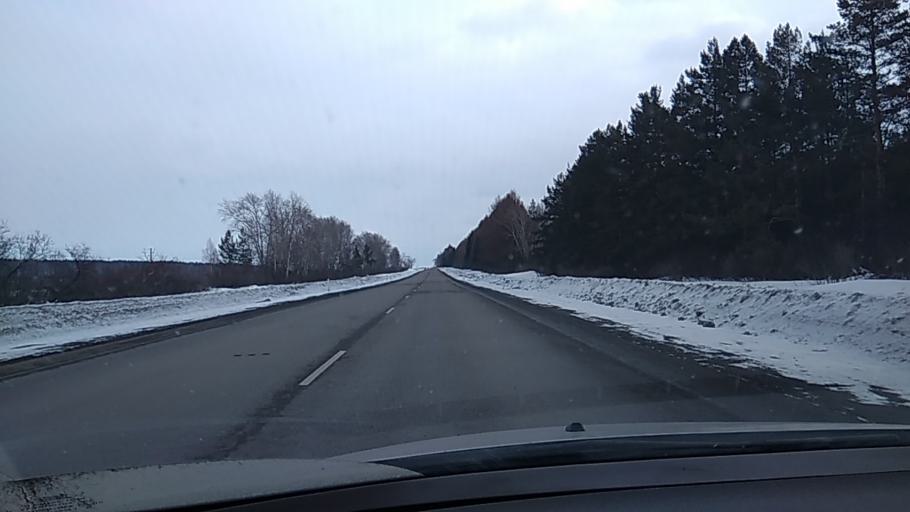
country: RU
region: Sverdlovsk
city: Dvurechensk
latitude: 56.6701
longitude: 61.1489
